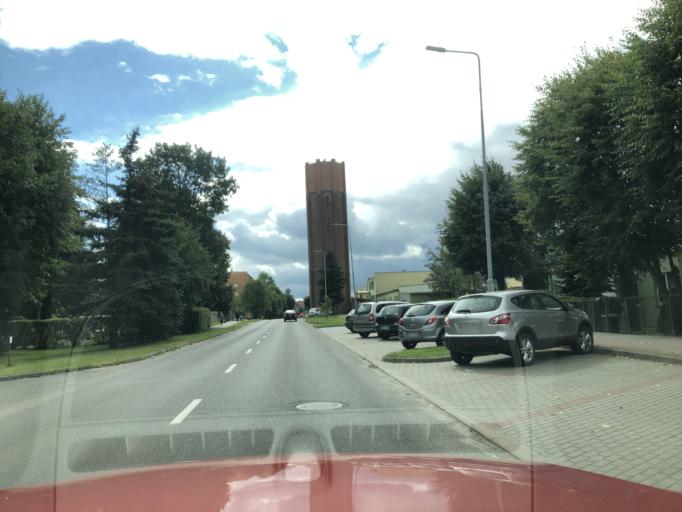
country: PL
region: Pomeranian Voivodeship
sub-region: Powiat czluchowski
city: Czluchow
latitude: 53.6647
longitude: 17.3531
